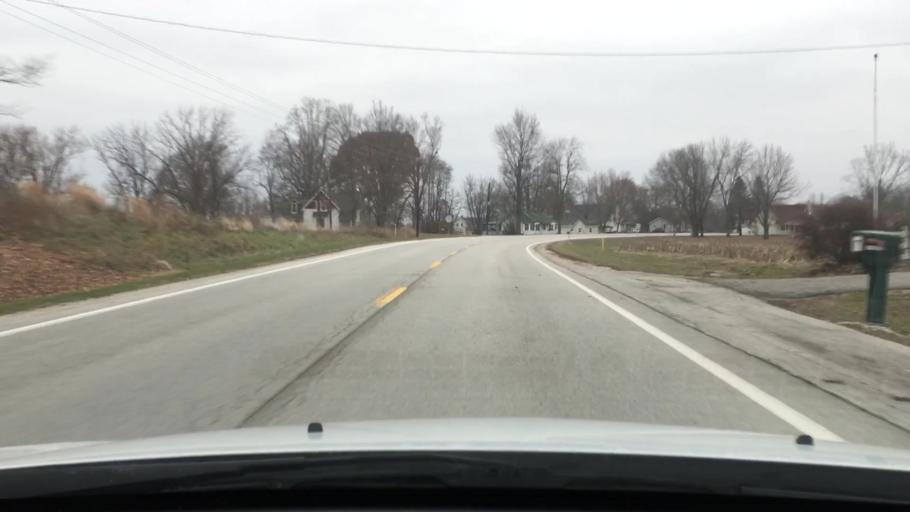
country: US
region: Illinois
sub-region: Pike County
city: Pittsfield
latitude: 39.5434
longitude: -90.9205
